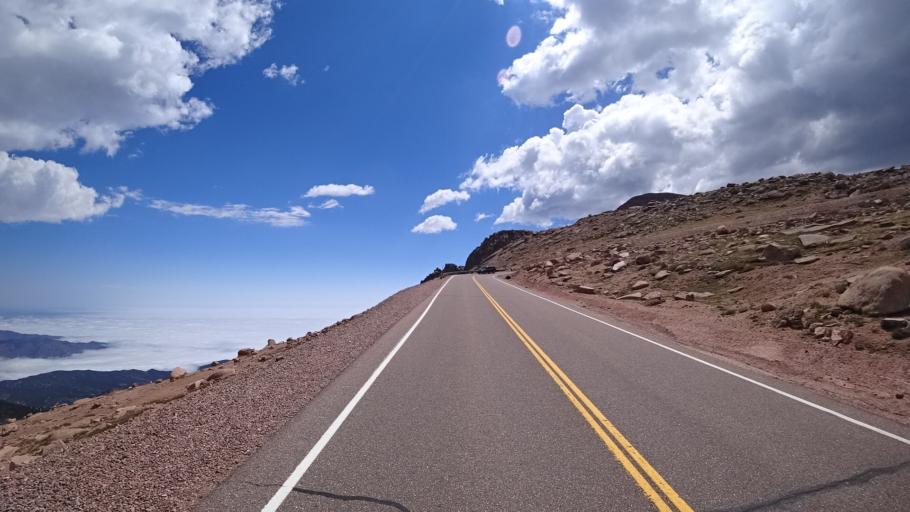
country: US
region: Colorado
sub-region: El Paso County
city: Cascade-Chipita Park
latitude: 38.8487
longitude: -105.0540
